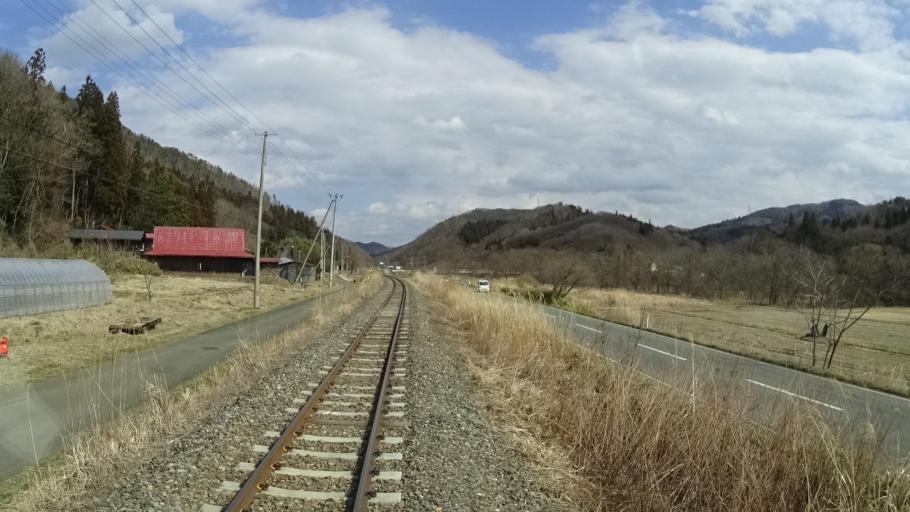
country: JP
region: Iwate
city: Hanamaki
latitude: 39.3618
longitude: 141.2740
